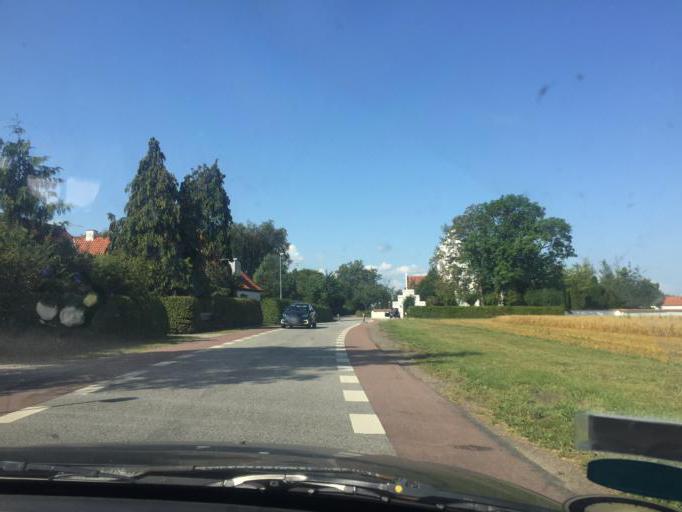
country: DK
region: Zealand
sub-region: Lolland Kommune
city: Maribo
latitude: 54.7983
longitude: 11.5167
